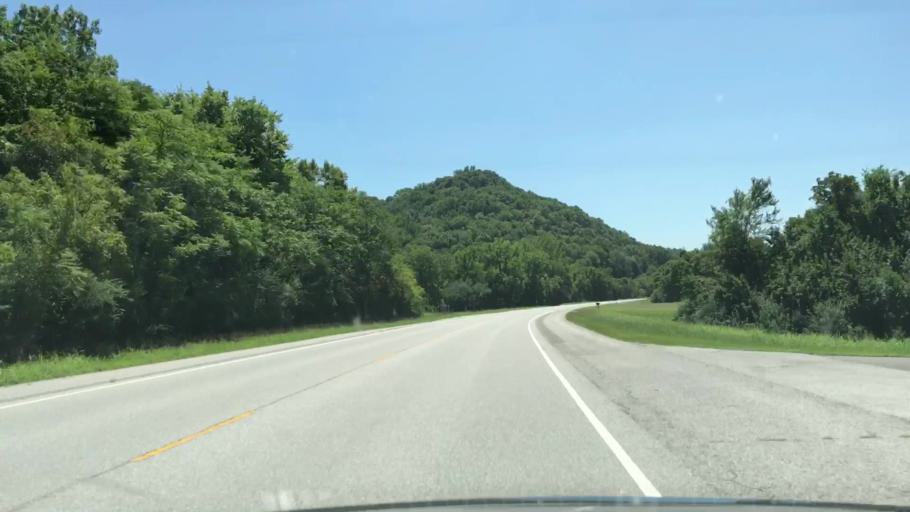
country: US
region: Tennessee
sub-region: Jackson County
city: Gainesboro
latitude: 36.4005
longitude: -85.6346
